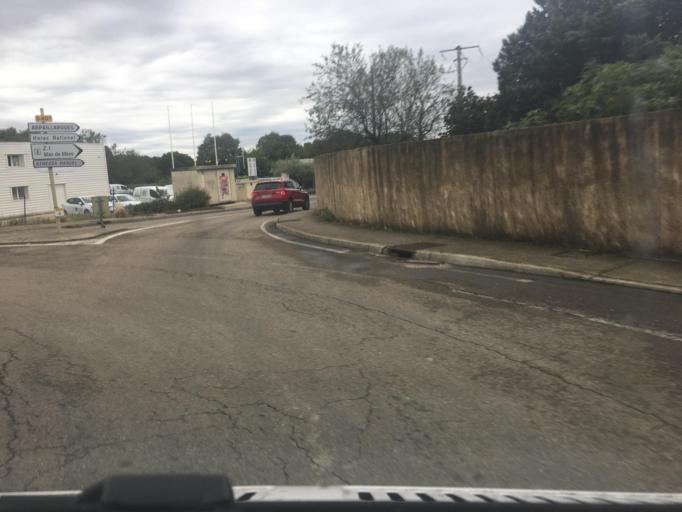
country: FR
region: Languedoc-Roussillon
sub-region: Departement du Gard
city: Uzes
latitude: 44.0197
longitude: 4.4016
